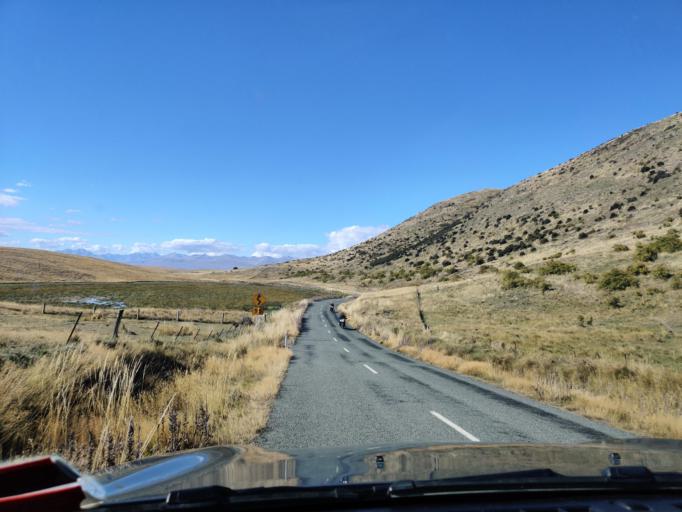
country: NZ
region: Canterbury
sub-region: Timaru District
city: Pleasant Point
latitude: -43.9801
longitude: 170.4607
